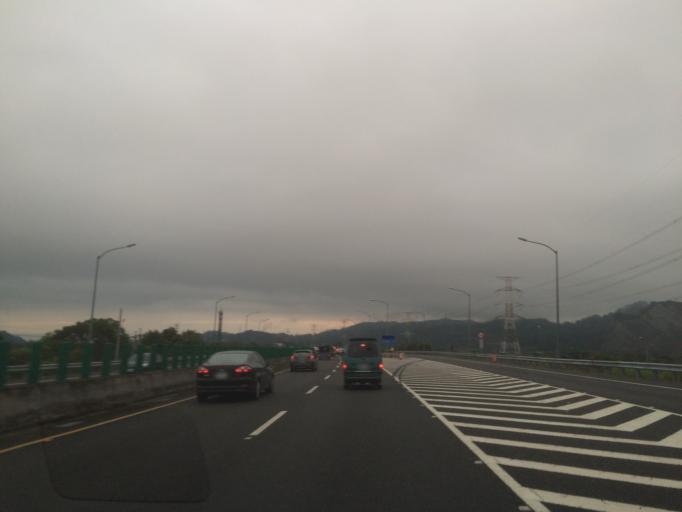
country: TW
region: Taiwan
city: Zhongxing New Village
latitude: 24.0020
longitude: 120.7374
